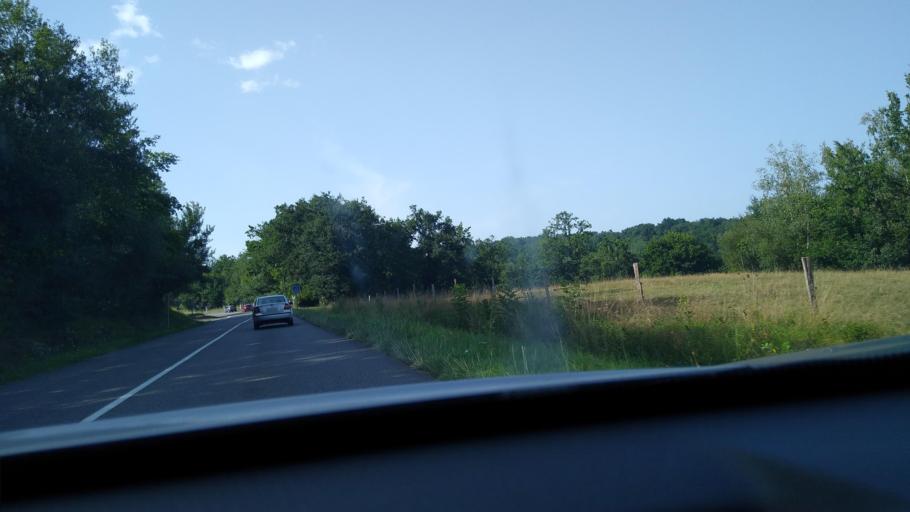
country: FR
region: Midi-Pyrenees
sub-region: Departement de la Haute-Garonne
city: Salies-du-Salat
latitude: 43.1006
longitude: 0.9505
